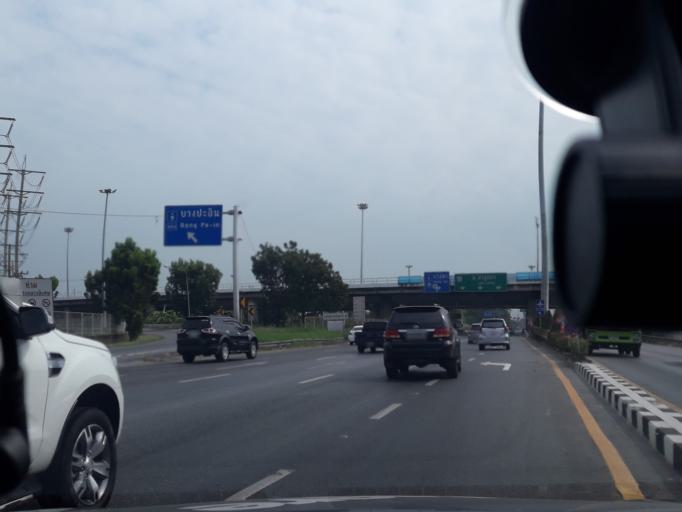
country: TH
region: Pathum Thani
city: Lam Luk Ka
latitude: 13.9337
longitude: 100.7070
